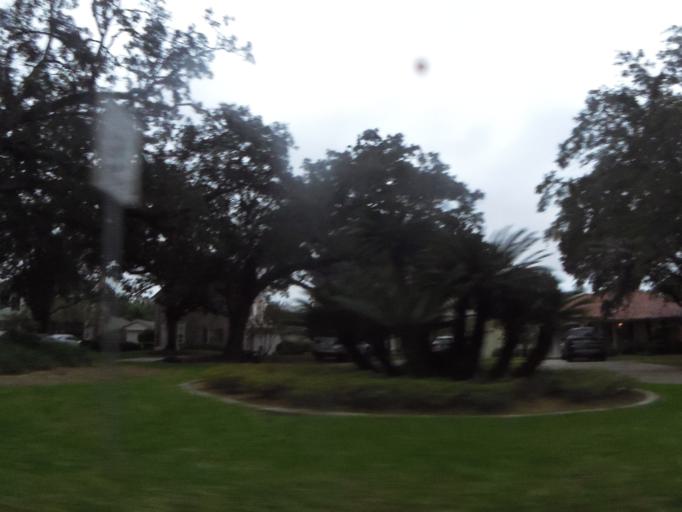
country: US
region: Florida
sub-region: Duval County
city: Jacksonville
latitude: 30.3033
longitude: -81.6557
